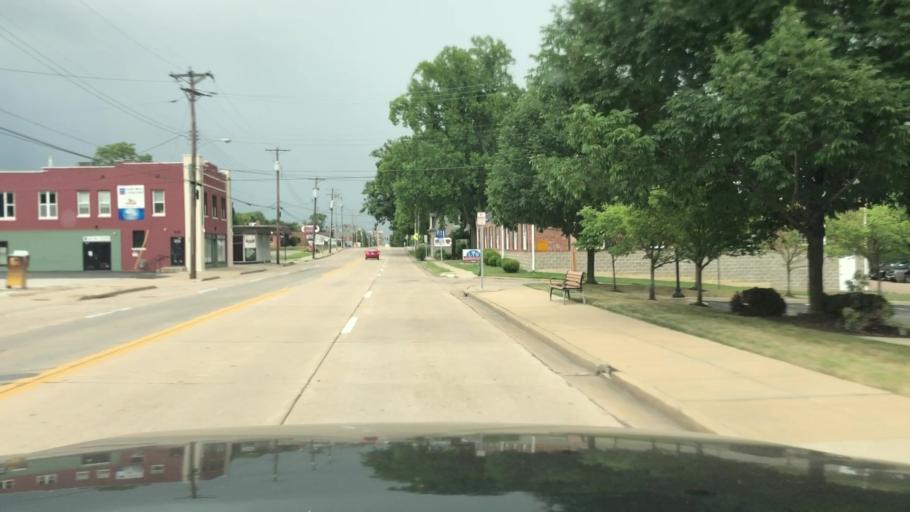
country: US
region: Missouri
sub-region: Saint Charles County
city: Saint Charles
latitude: 38.7834
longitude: -90.4942
